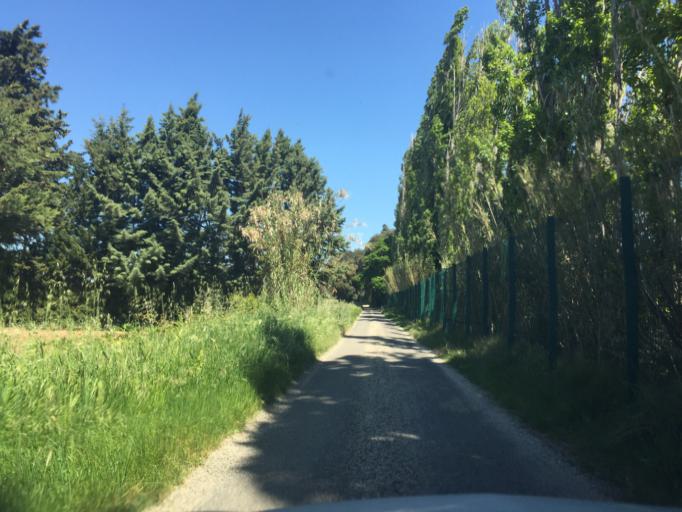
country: FR
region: Provence-Alpes-Cote d'Azur
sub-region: Departement du Vaucluse
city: Caderousse
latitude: 44.0973
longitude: 4.7940
